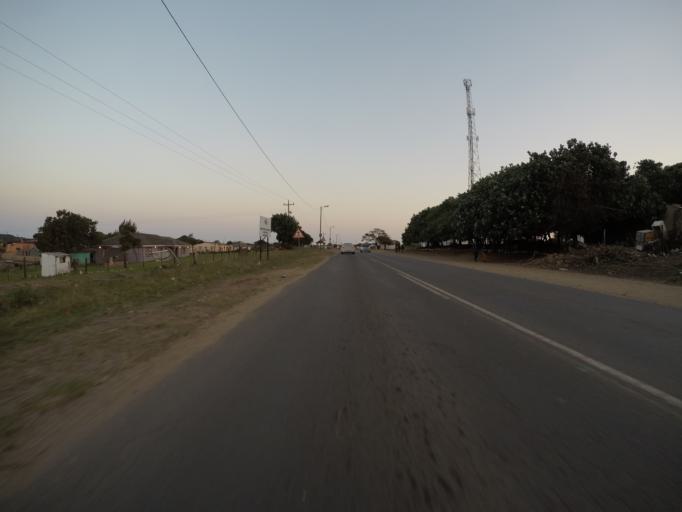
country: ZA
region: KwaZulu-Natal
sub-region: uThungulu District Municipality
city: Richards Bay
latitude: -28.7602
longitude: 32.1326
